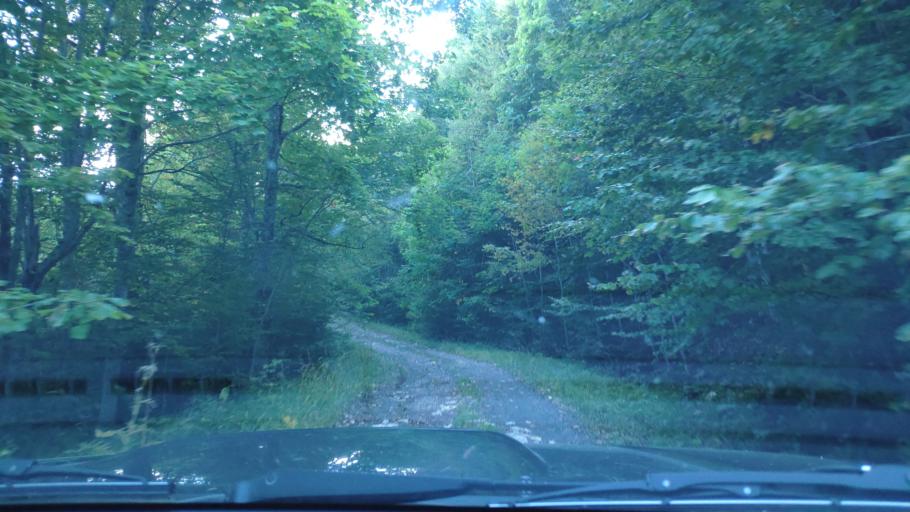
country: AL
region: Korce
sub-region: Rrethi i Devollit
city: Miras
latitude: 40.3617
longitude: 20.8957
